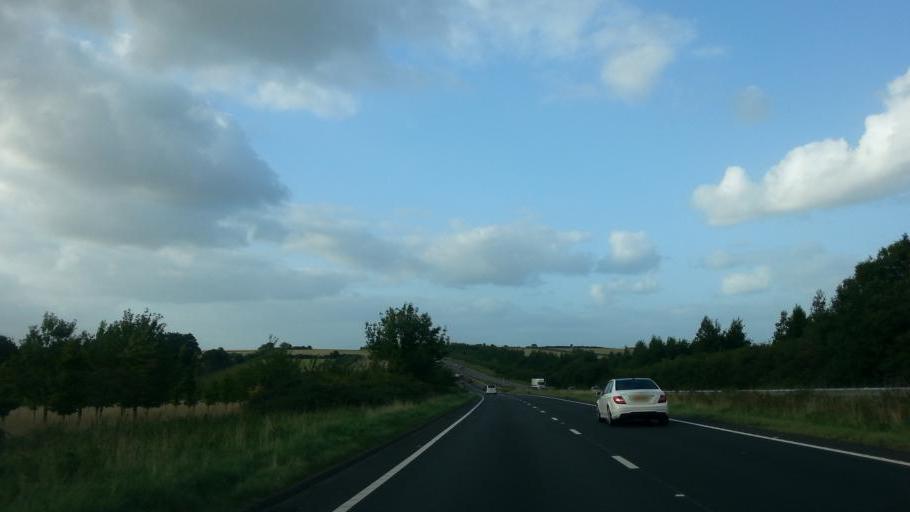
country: GB
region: England
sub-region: Hampshire
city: Overton
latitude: 51.1965
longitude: -1.3369
